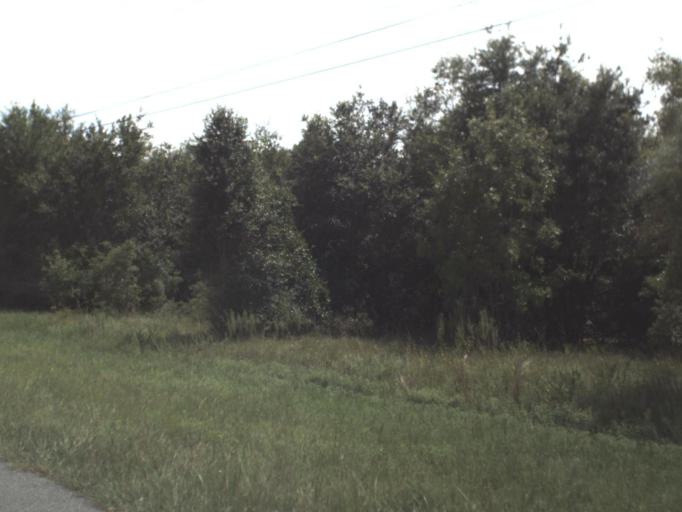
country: US
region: Florida
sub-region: Citrus County
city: Hernando
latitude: 28.9143
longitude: -82.3755
